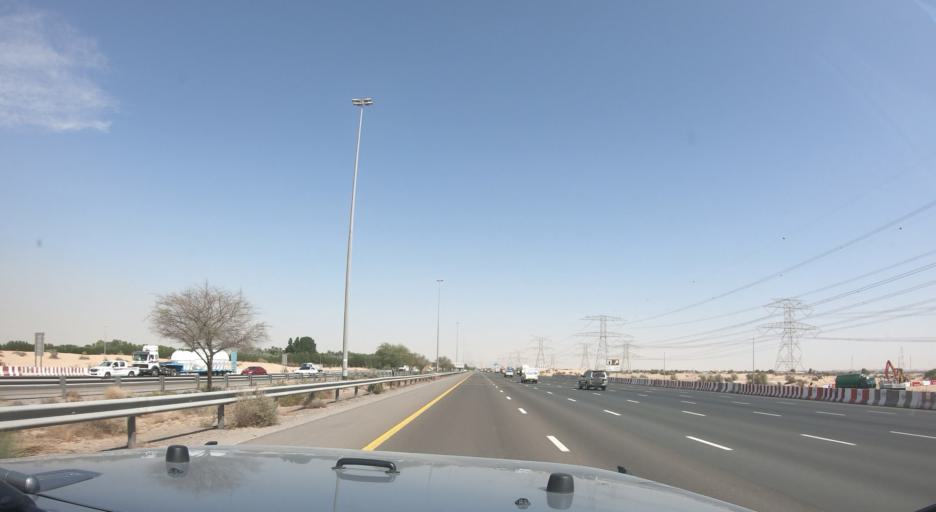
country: AE
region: Ash Shariqah
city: Sharjah
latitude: 25.1856
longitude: 55.5255
